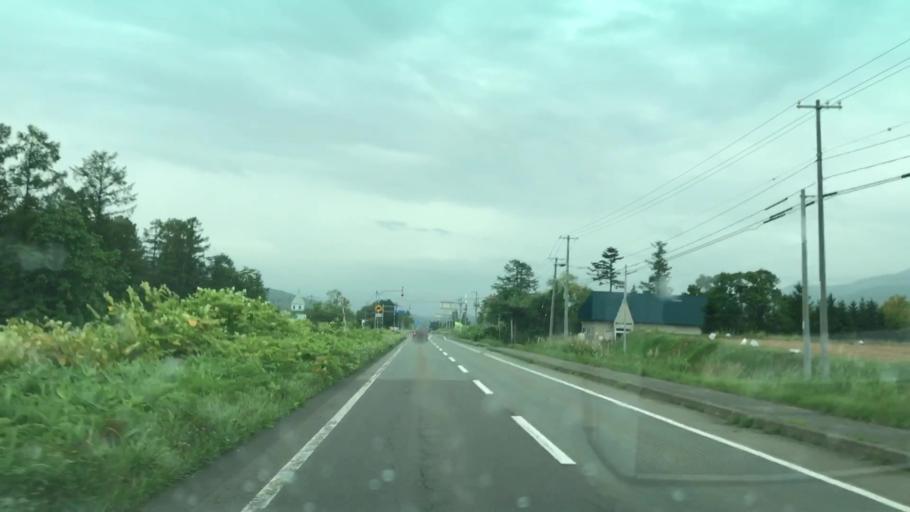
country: JP
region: Hokkaido
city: Niseko Town
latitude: 42.7602
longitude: 140.4781
